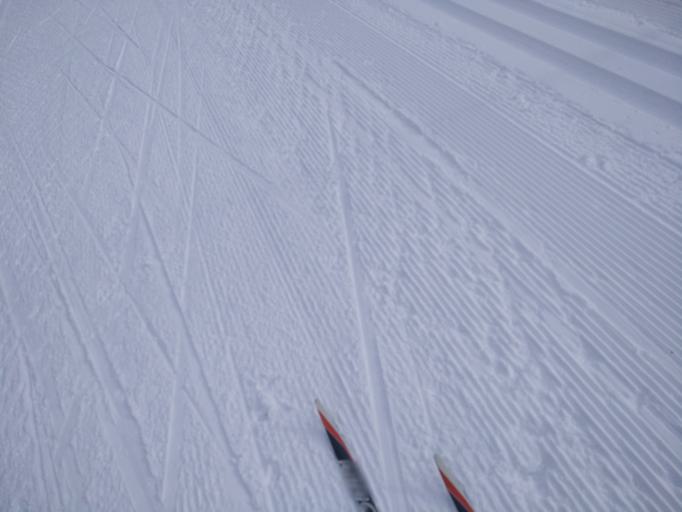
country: FI
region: Northern Ostrobothnia
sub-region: Koillismaa
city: Taivalkoski
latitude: 65.6550
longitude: 27.5708
